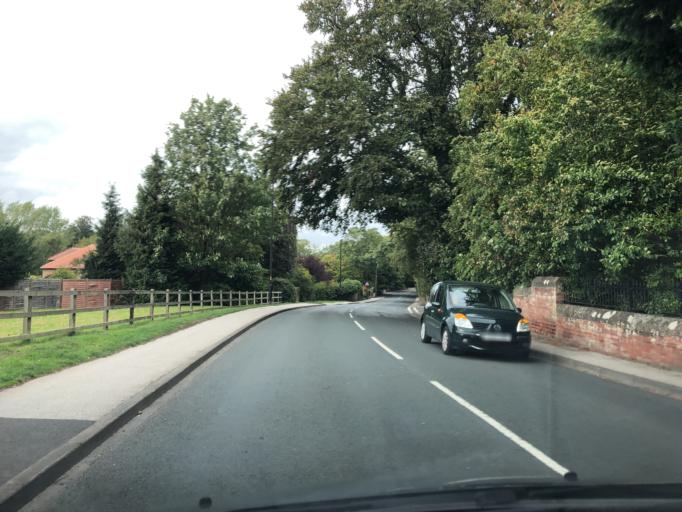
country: GB
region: England
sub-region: North Yorkshire
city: Ripon
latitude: 54.1309
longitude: -1.5279
